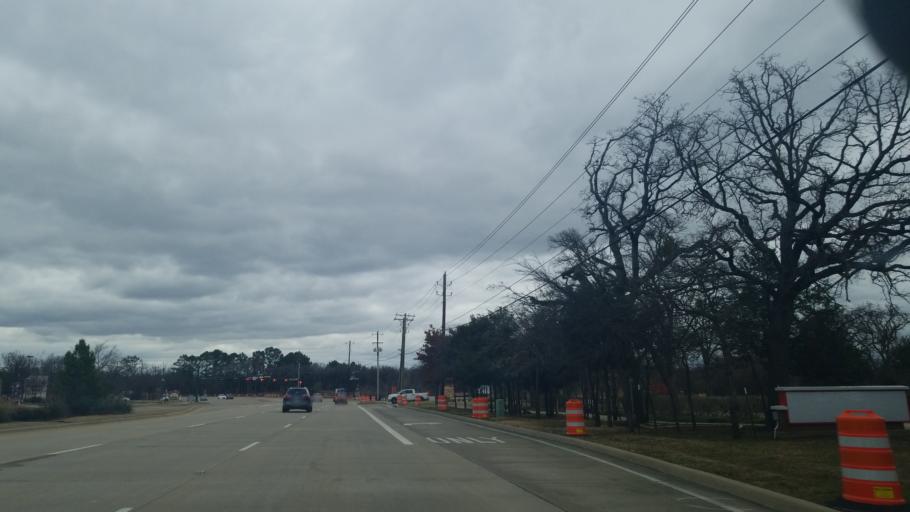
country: US
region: Texas
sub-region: Denton County
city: Flower Mound
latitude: 33.0455
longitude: -97.0693
